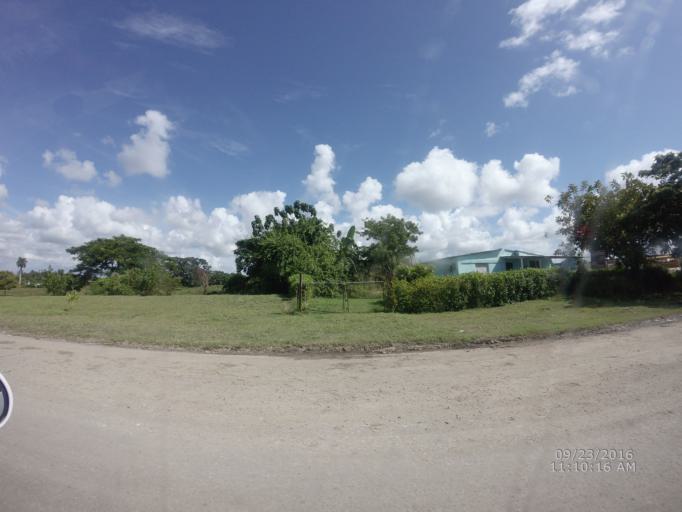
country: CU
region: La Habana
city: Arroyo Naranjo
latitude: 23.0198
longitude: -82.2545
